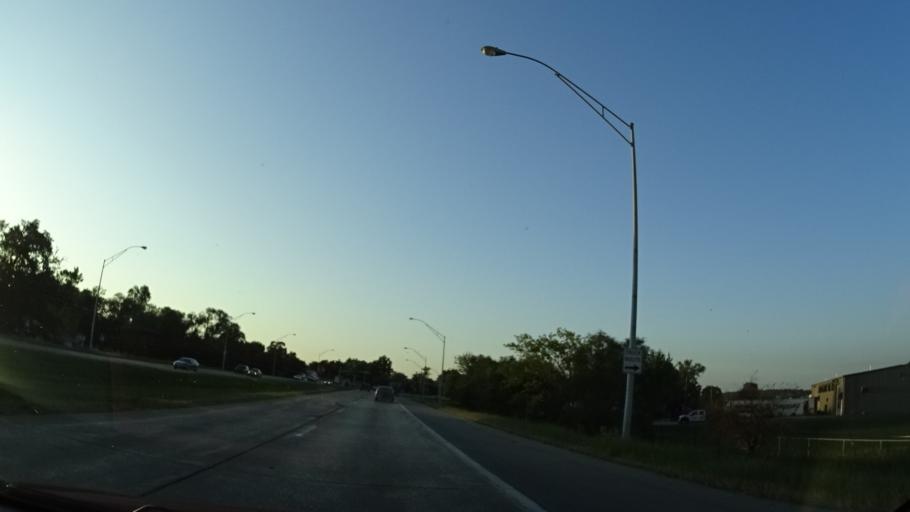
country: US
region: Iowa
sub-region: Pottawattamie County
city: Council Bluffs
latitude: 41.2420
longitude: -95.8521
